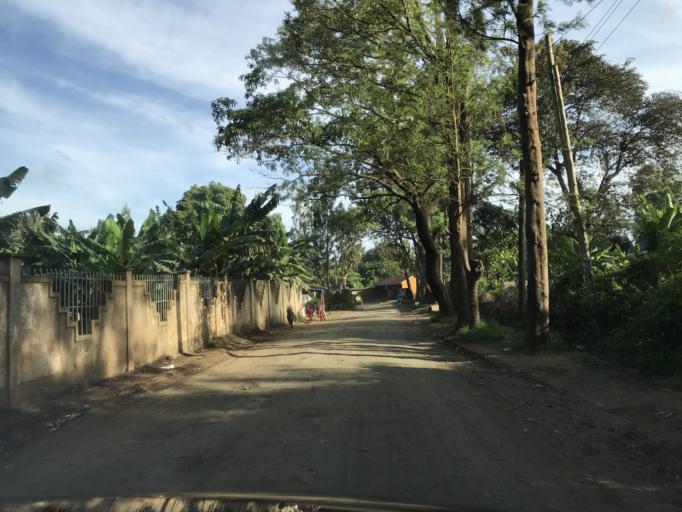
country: TZ
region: Arusha
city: Arusha
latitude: -3.3861
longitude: 36.7174
